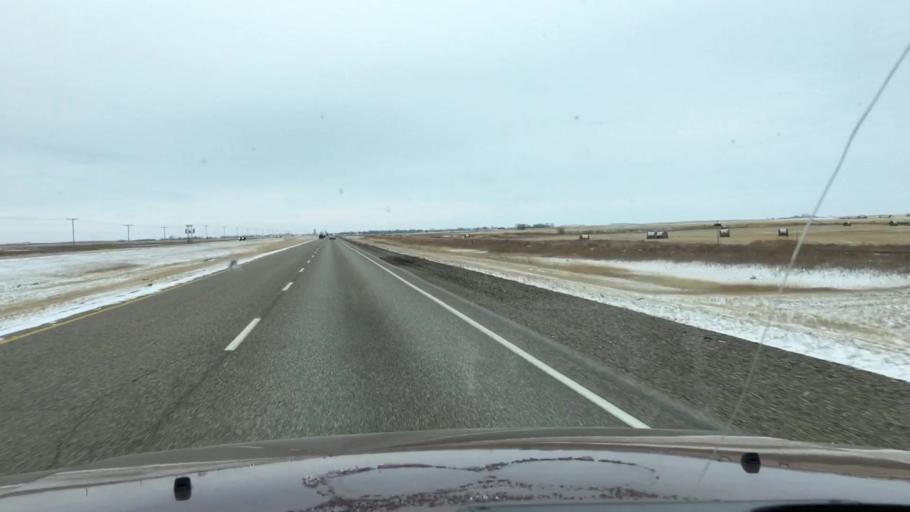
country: CA
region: Saskatchewan
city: Watrous
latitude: 51.0815
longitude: -105.8496
